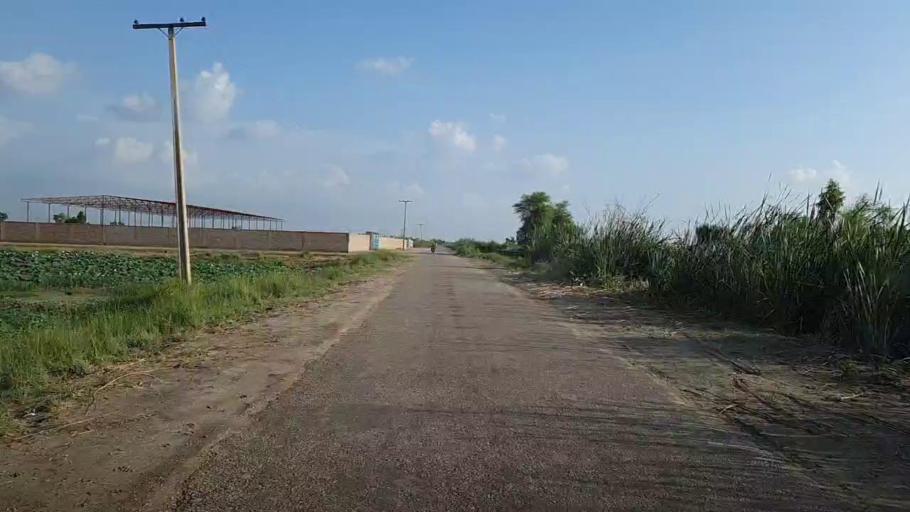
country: PK
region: Sindh
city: Hingorja
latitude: 27.0980
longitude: 68.4023
